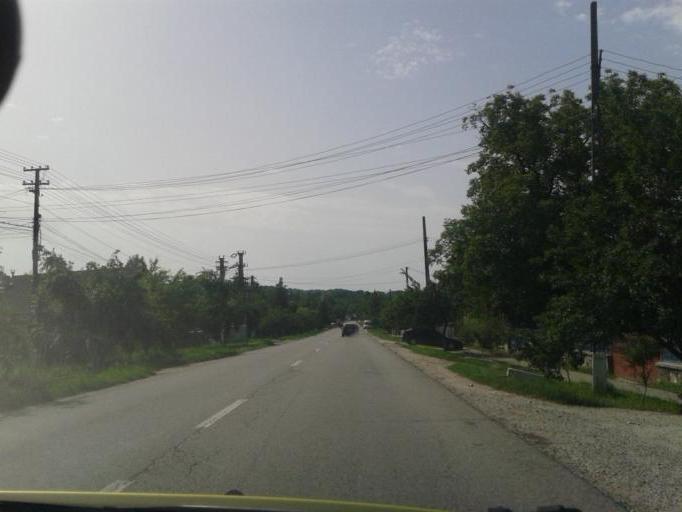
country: RO
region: Valcea
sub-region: Comuna Pietrari
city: Pietrari
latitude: 45.1075
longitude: 24.1178
